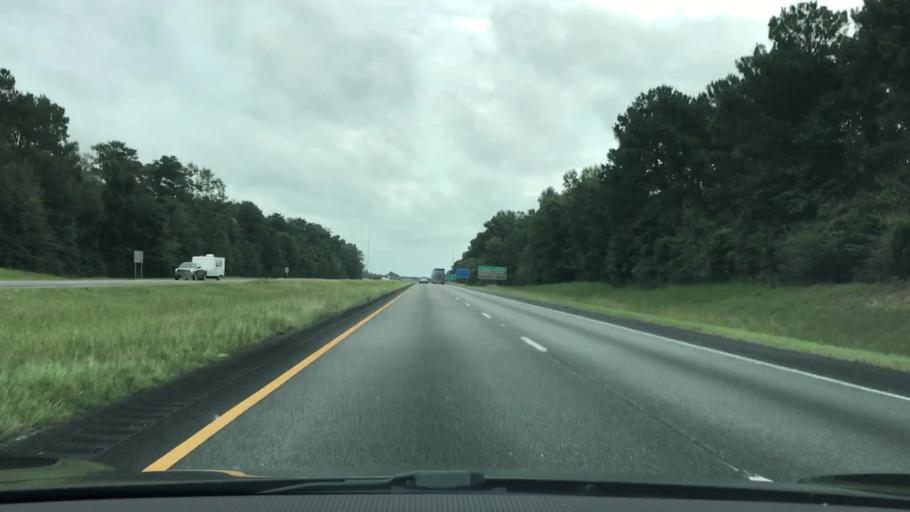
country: US
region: Alabama
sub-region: Macon County
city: Tuskegee
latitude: 32.4449
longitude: -85.8055
